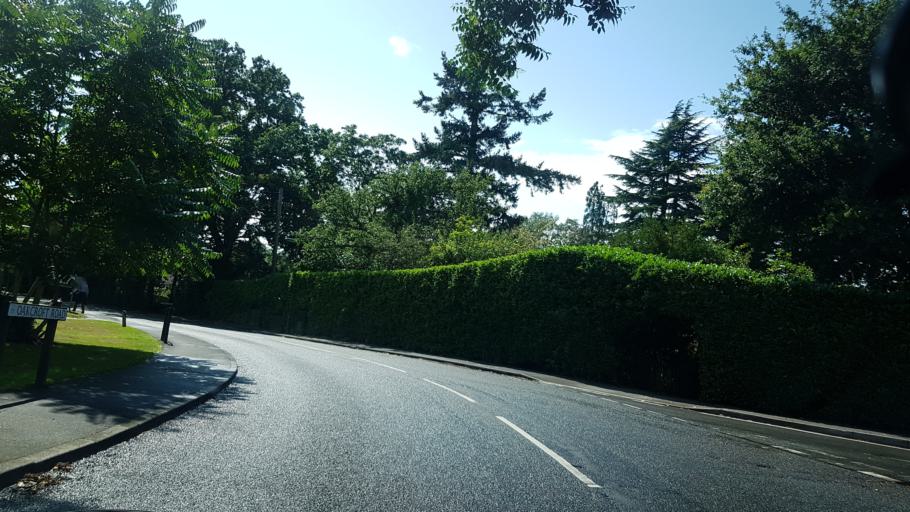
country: GB
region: England
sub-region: Surrey
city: West Byfleet
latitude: 51.3296
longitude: -0.5100
